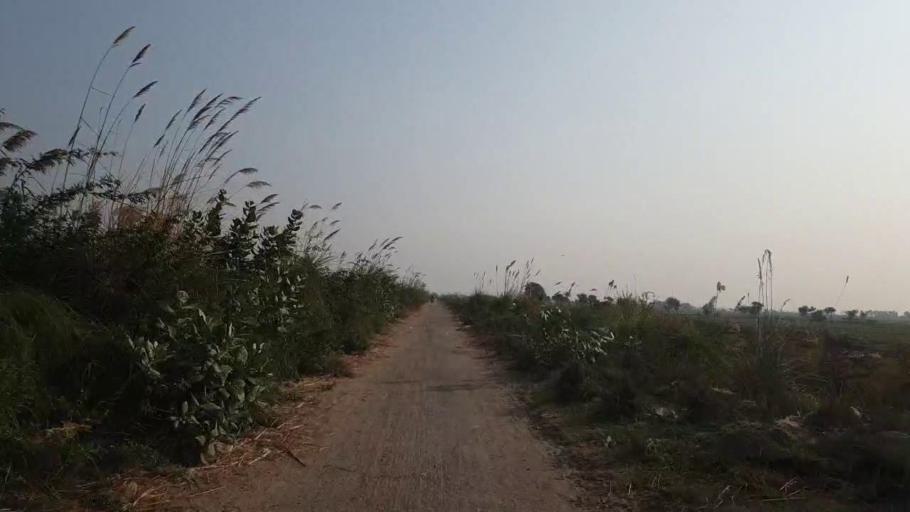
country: PK
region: Sindh
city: Tando Muhammad Khan
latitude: 25.1000
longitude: 68.3541
